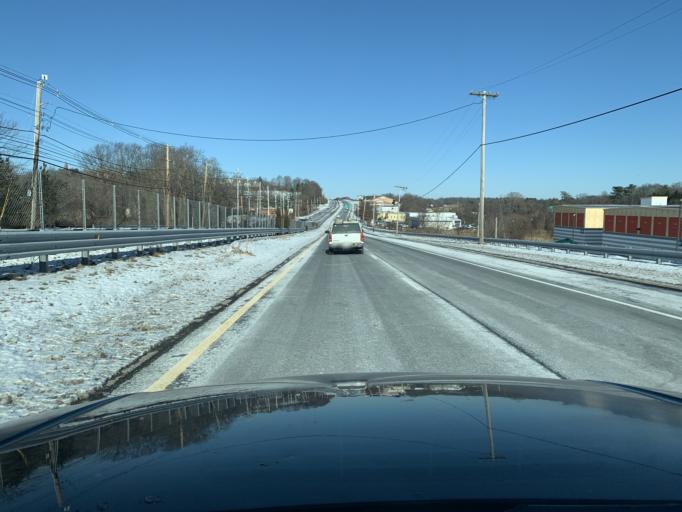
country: US
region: Massachusetts
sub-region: Essex County
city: Danvers
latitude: 42.5711
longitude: -70.9728
